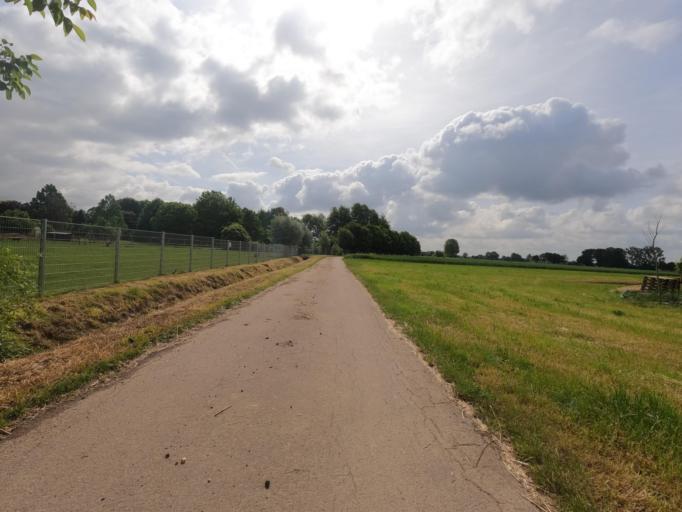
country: DE
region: North Rhine-Westphalia
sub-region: Regierungsbezirk Koln
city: Heinsberg
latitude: 51.0889
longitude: 6.1176
